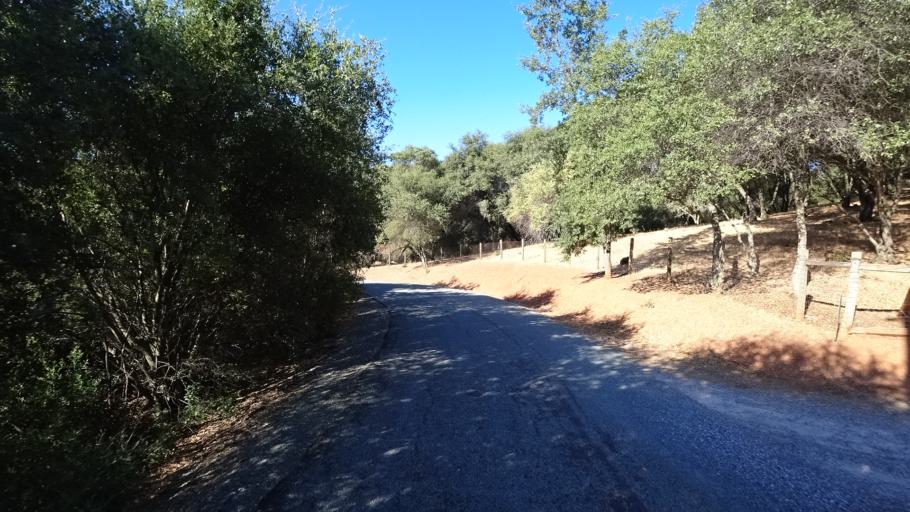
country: US
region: California
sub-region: Calaveras County
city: San Andreas
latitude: 38.2477
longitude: -120.7066
